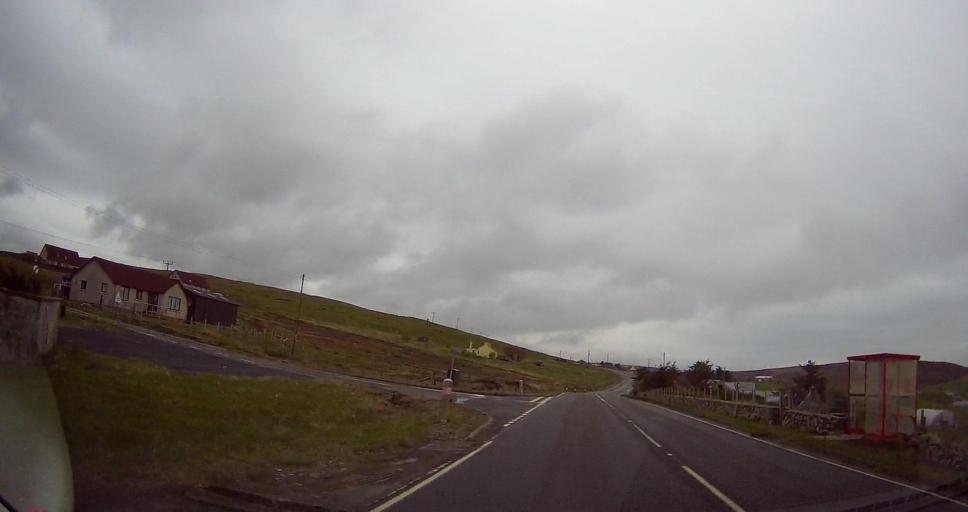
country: GB
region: Scotland
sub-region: Shetland Islands
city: Lerwick
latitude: 60.2349
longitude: -1.2331
